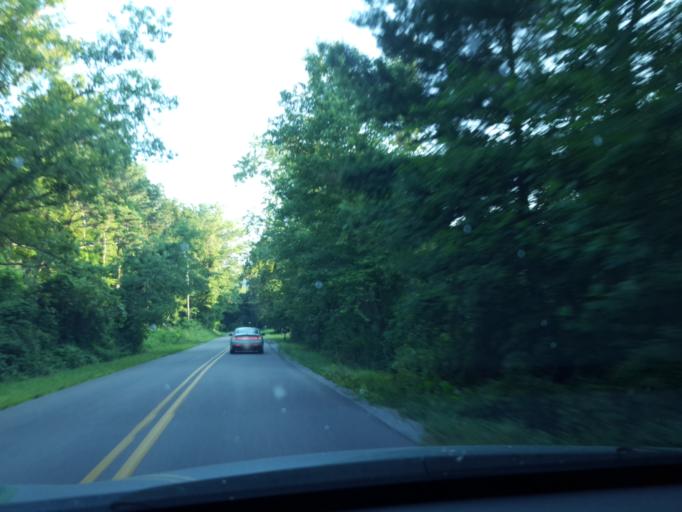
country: US
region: Virginia
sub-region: Augusta County
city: Lyndhurst
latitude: 37.9660
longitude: -78.9602
